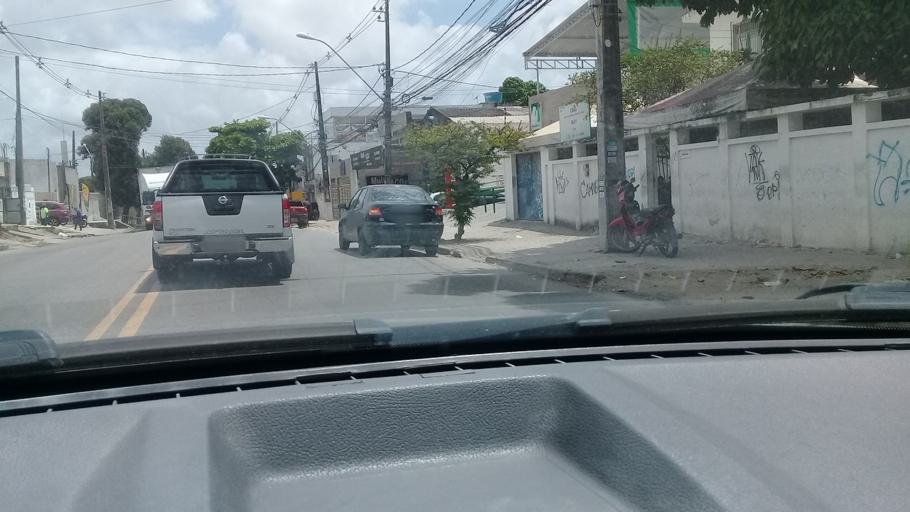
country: BR
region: Pernambuco
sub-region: Jaboatao Dos Guararapes
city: Jaboatao dos Guararapes
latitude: -8.1128
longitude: -34.9385
